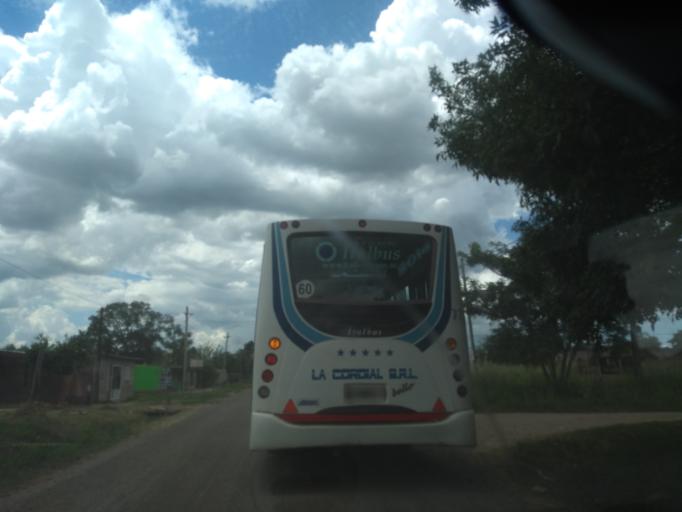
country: AR
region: Chaco
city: Fontana
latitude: -27.4062
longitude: -59.0455
